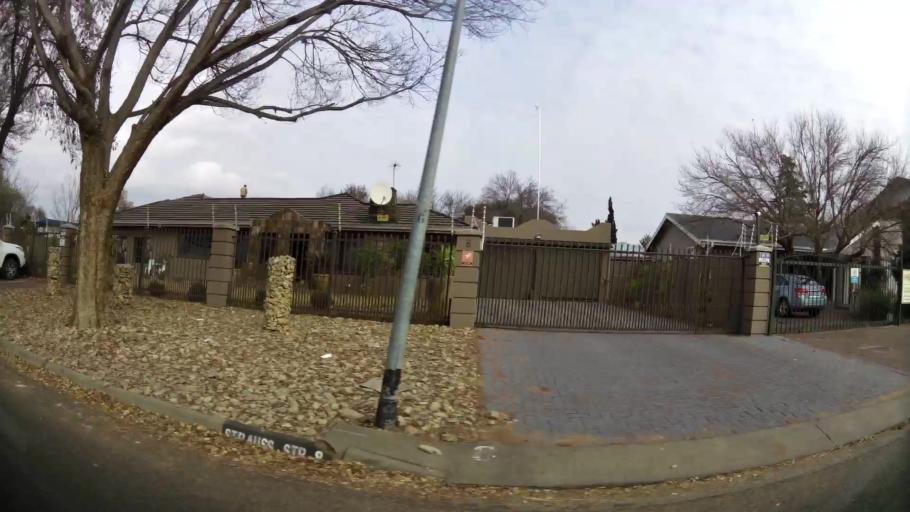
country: ZA
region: Orange Free State
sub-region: Mangaung Metropolitan Municipality
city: Bloemfontein
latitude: -29.1208
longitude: 26.1851
